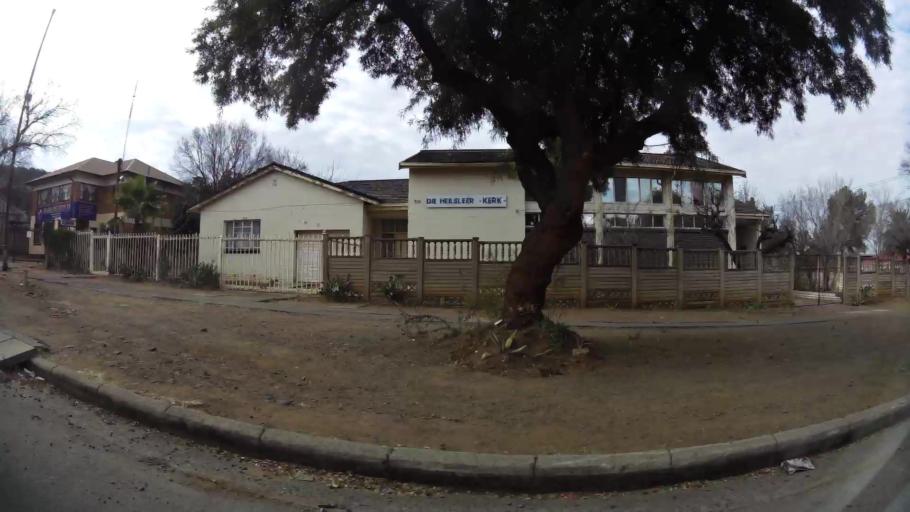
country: ZA
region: Orange Free State
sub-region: Mangaung Metropolitan Municipality
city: Bloemfontein
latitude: -29.1104
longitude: 26.2286
